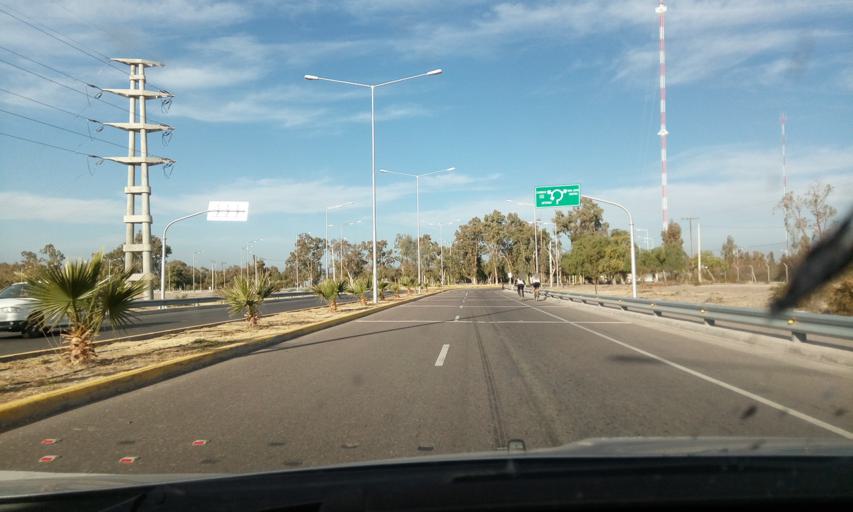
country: AR
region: San Juan
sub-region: Departamento de Rivadavia
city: Rivadavia
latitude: -31.5153
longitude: -68.6326
